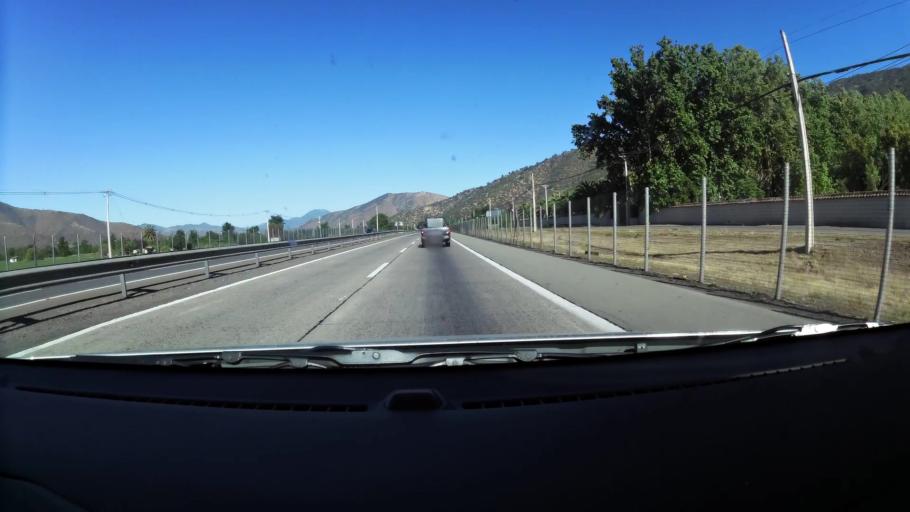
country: CL
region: Santiago Metropolitan
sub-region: Provincia de Chacabuco
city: Lampa
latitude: -33.4028
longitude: -71.0962
